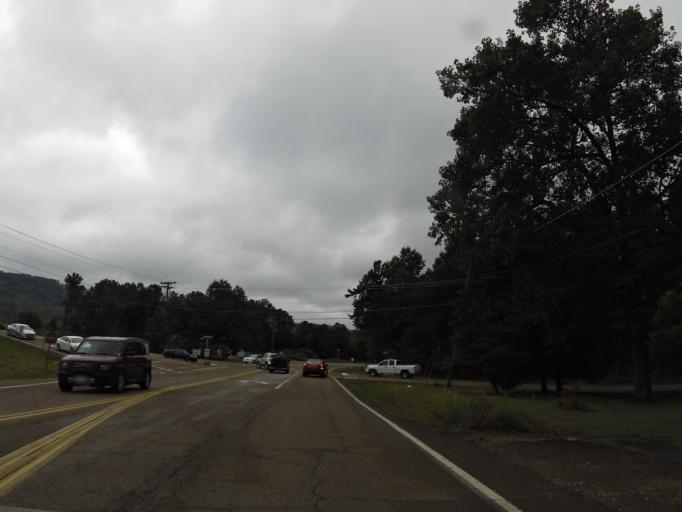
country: US
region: Tennessee
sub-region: Hamilton County
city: Collegedale
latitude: 35.1189
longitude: -85.0472
